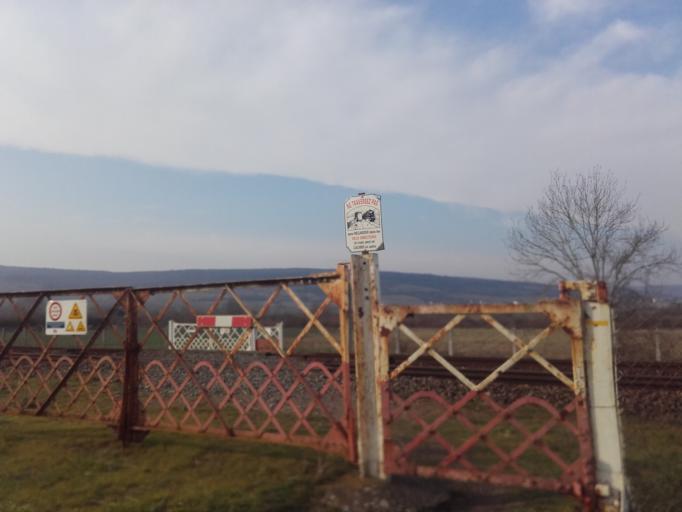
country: FR
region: Bourgogne
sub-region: Departement de Saone-et-Loire
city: Chagny
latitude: 46.9149
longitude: 4.7346
